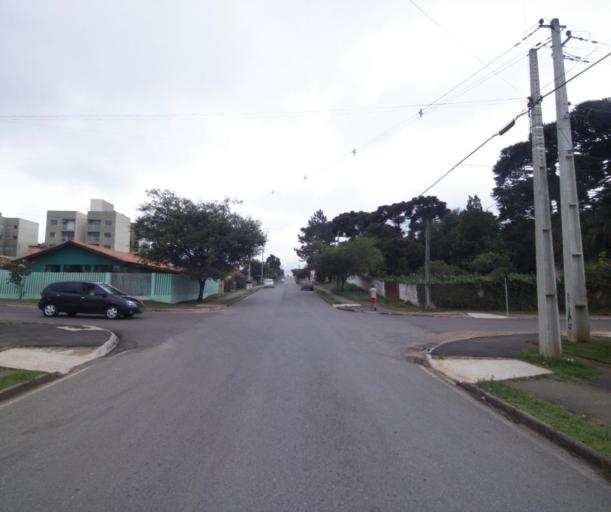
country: BR
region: Parana
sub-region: Quatro Barras
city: Quatro Barras
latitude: -25.3640
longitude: -49.1095
